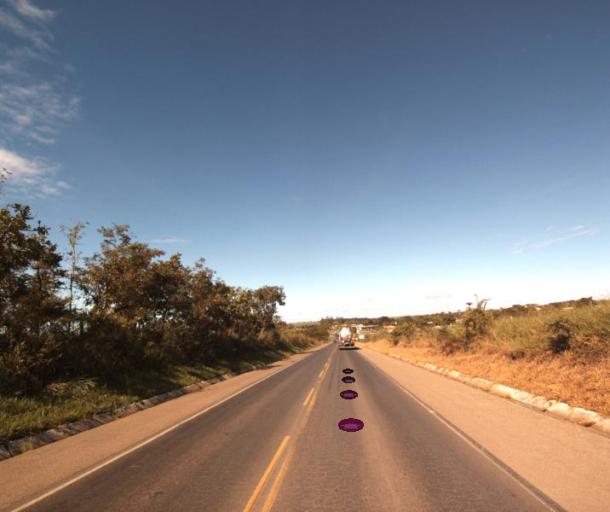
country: BR
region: Goias
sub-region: Itapaci
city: Itapaci
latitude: -14.8603
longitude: -49.3242
